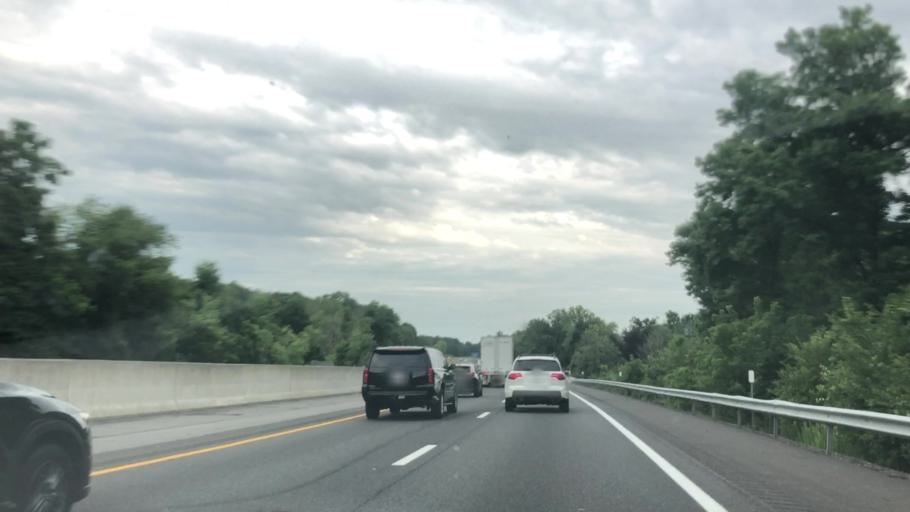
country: US
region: New York
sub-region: Ulster County
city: Clintondale
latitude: 41.6754
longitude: -74.0807
